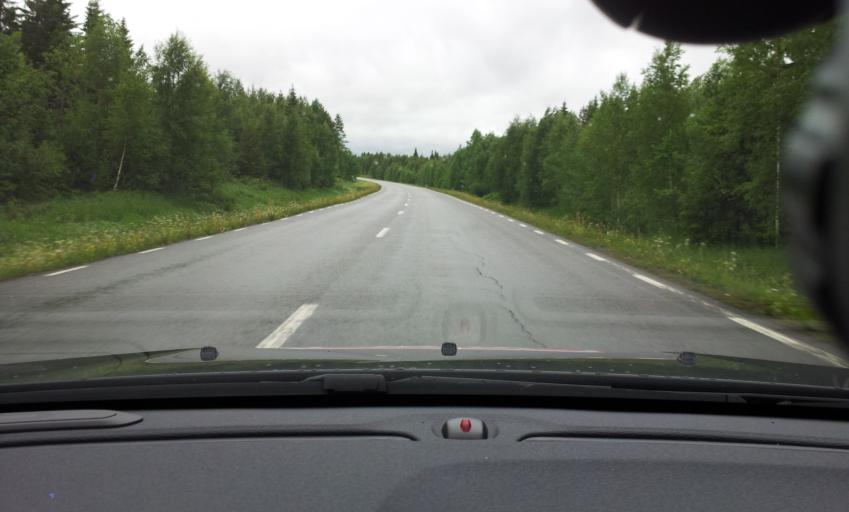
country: SE
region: Jaemtland
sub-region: Krokoms Kommun
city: Krokom
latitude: 63.3821
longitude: 14.5074
